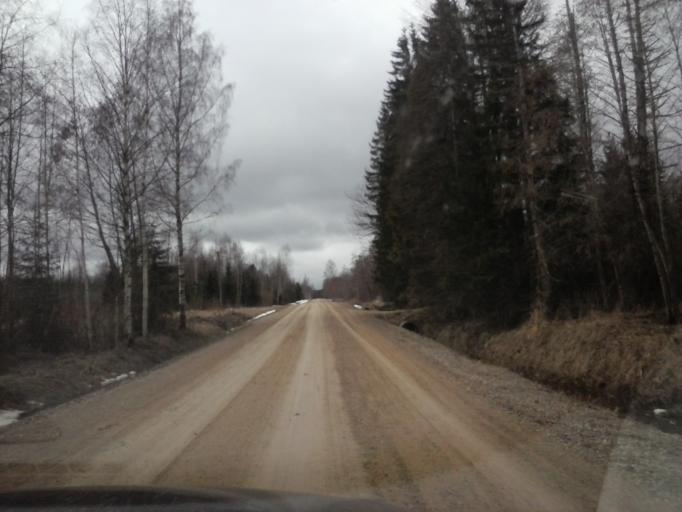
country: EE
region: Jogevamaa
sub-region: Mustvee linn
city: Mustvee
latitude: 59.0835
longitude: 26.8645
